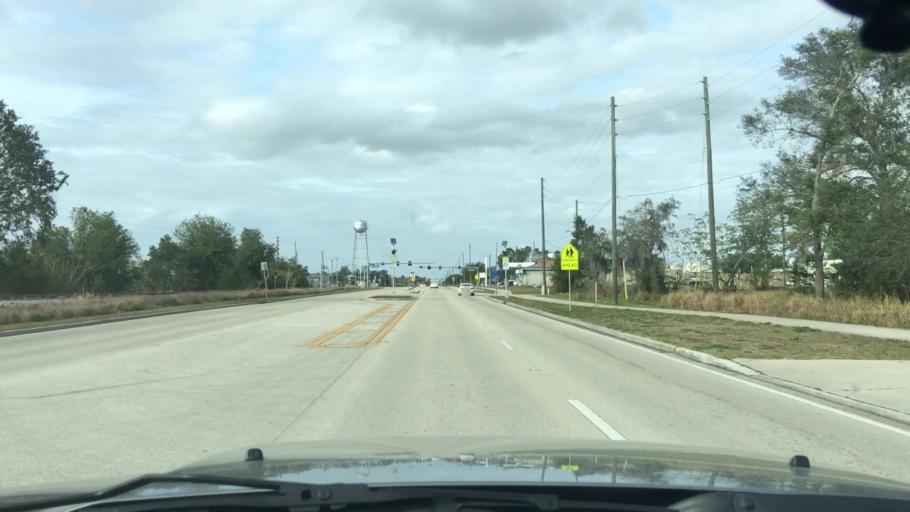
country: US
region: Florida
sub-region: Highlands County
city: Sebring
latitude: 27.4835
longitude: -81.4334
